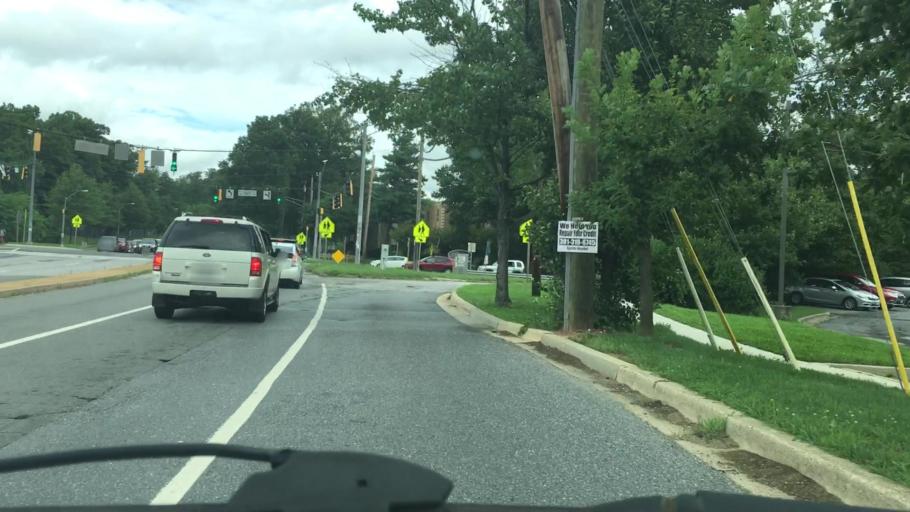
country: US
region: Maryland
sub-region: Prince George's County
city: Glenn Dale
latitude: 38.9902
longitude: -76.8358
